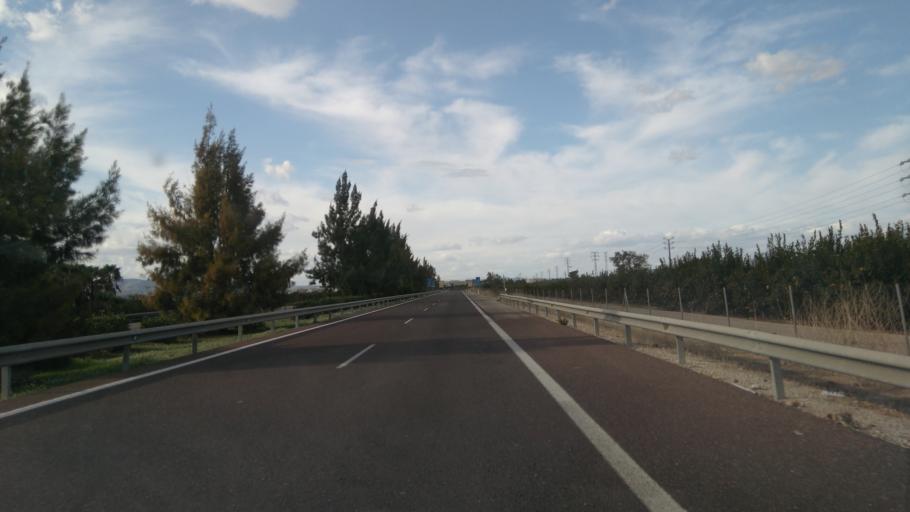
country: ES
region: Valencia
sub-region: Provincia de Valencia
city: L'Alcudia
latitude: 39.1832
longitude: -0.4883
